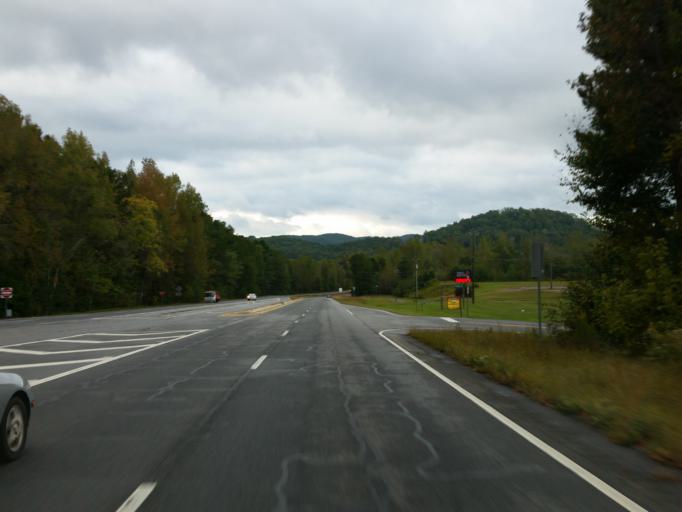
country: US
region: Georgia
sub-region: Bartow County
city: Emerson
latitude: 34.1046
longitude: -84.7467
